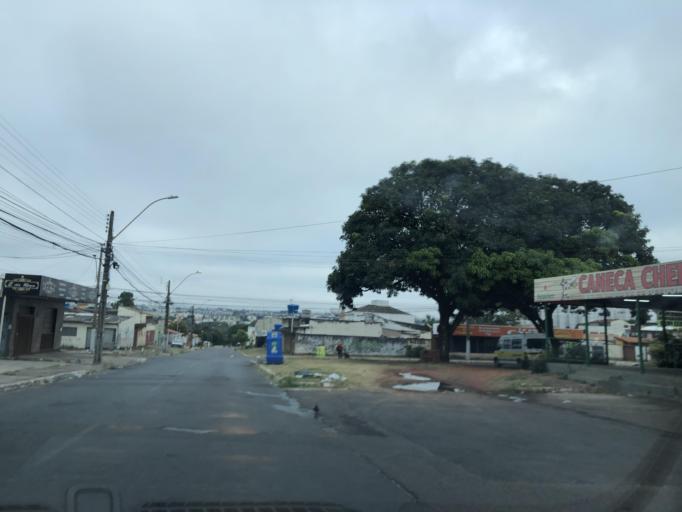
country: BR
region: Federal District
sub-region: Brasilia
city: Brasilia
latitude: -15.8155
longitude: -48.0685
